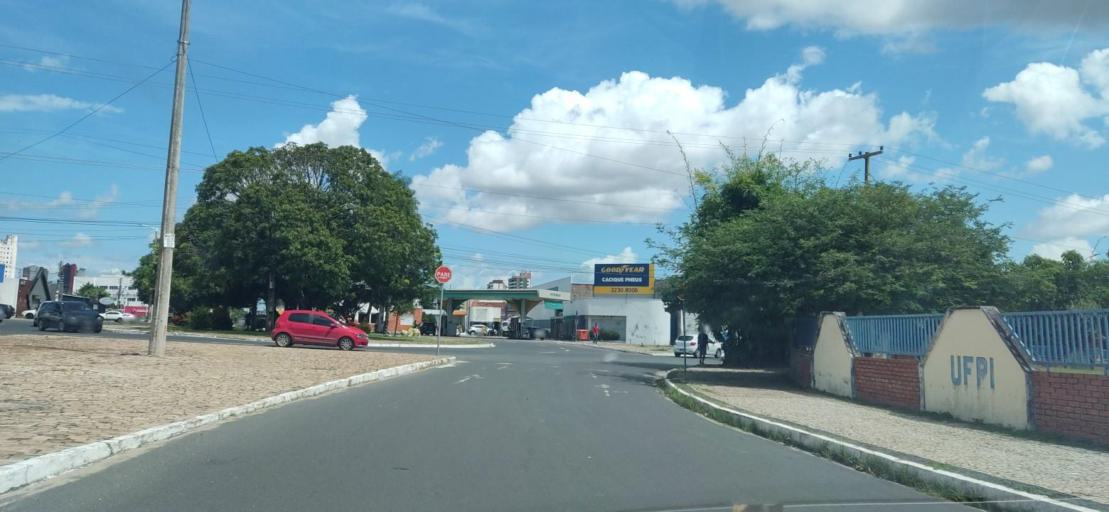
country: BR
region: Piaui
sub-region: Teresina
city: Teresina
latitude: -5.0618
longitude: -42.7948
